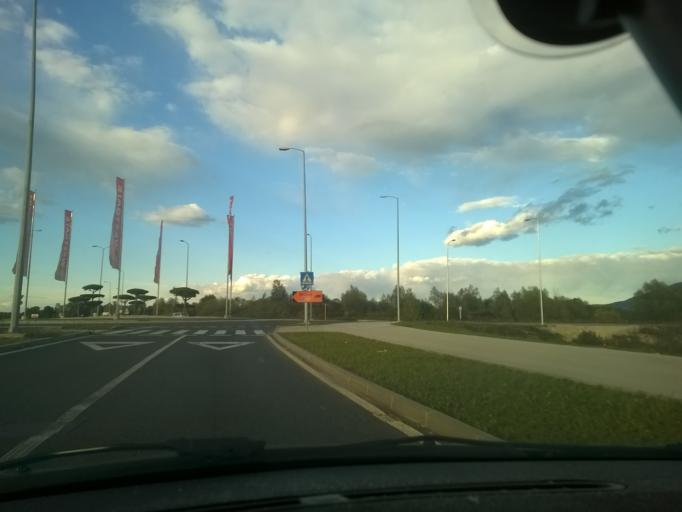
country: HR
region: Zagrebacka
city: Zapresic
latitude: 45.8780
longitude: 15.8194
